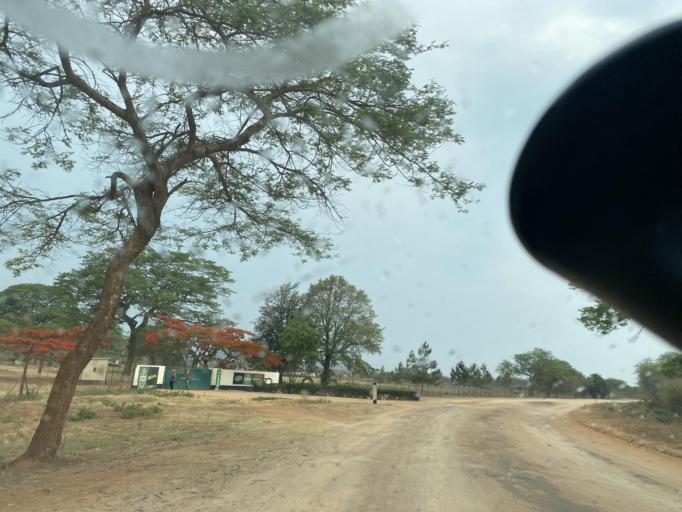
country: ZM
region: Lusaka
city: Lusaka
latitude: -15.2853
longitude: 28.2971
